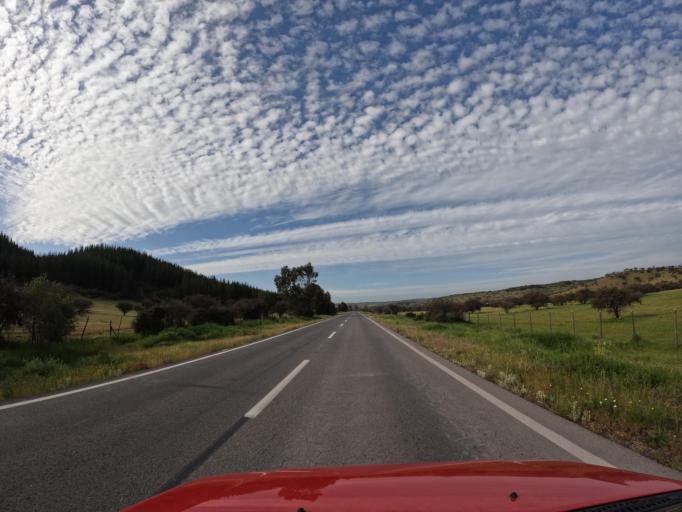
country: CL
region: O'Higgins
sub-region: Provincia de Colchagua
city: Santa Cruz
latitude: -34.3036
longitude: -71.7354
